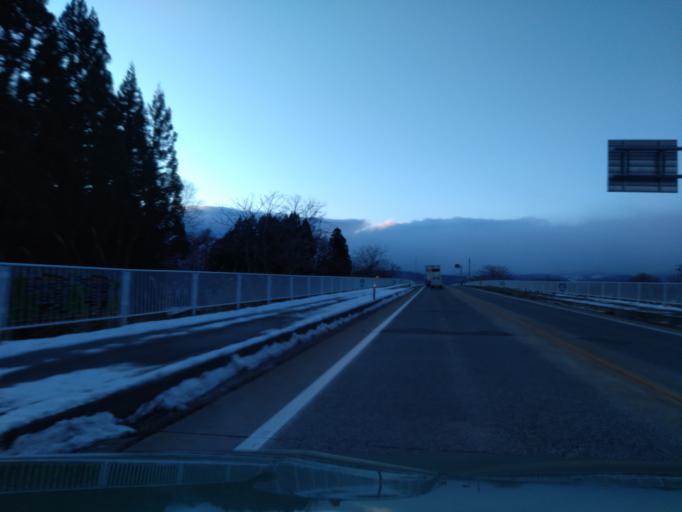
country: JP
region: Iwate
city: Shizukuishi
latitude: 39.6902
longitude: 140.9892
